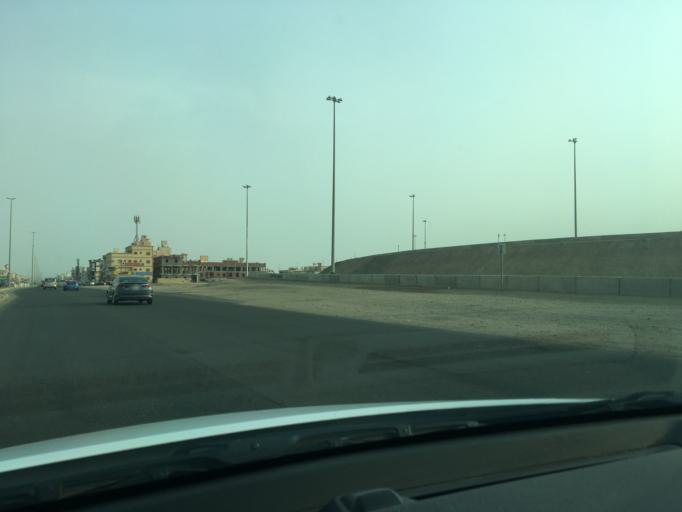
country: SA
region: Makkah
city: Jeddah
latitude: 21.7628
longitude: 39.1829
